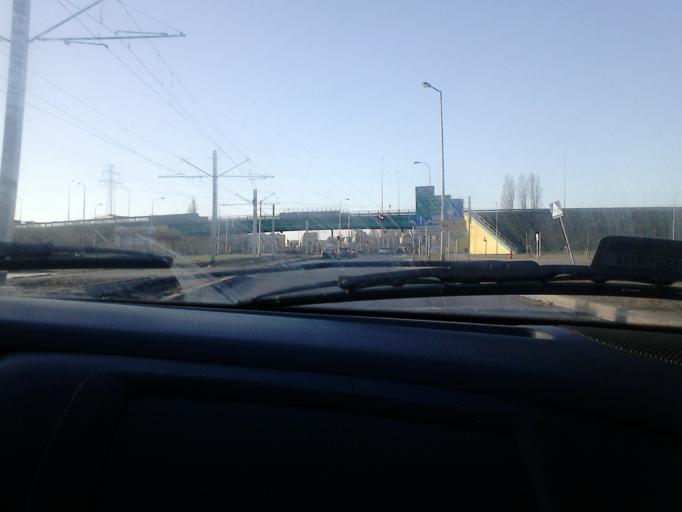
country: PL
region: Pomeranian Voivodeship
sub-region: Gdansk
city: Gdansk
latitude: 54.3610
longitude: 18.6938
